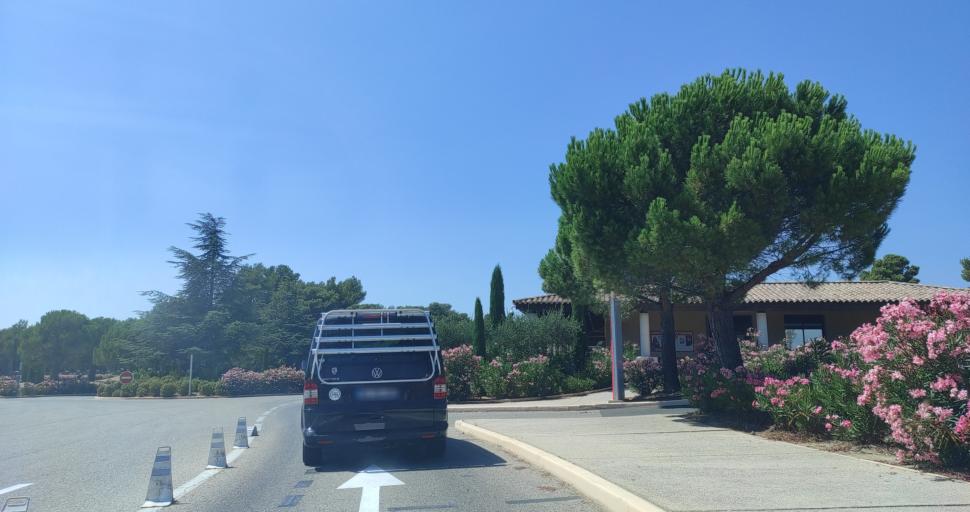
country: FR
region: Provence-Alpes-Cote d'Azur
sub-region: Departement du Var
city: Le Castellet
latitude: 43.2489
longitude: 5.7889
